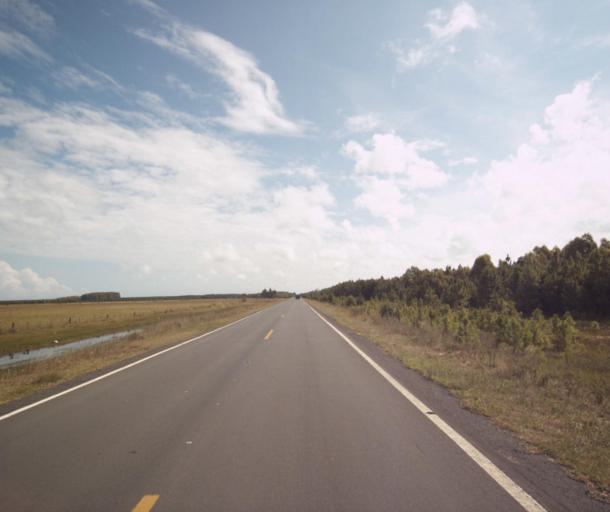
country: BR
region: Rio Grande do Sul
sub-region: Sao Lourenco Do Sul
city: Sao Lourenco do Sul
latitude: -31.4519
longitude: -51.2144
